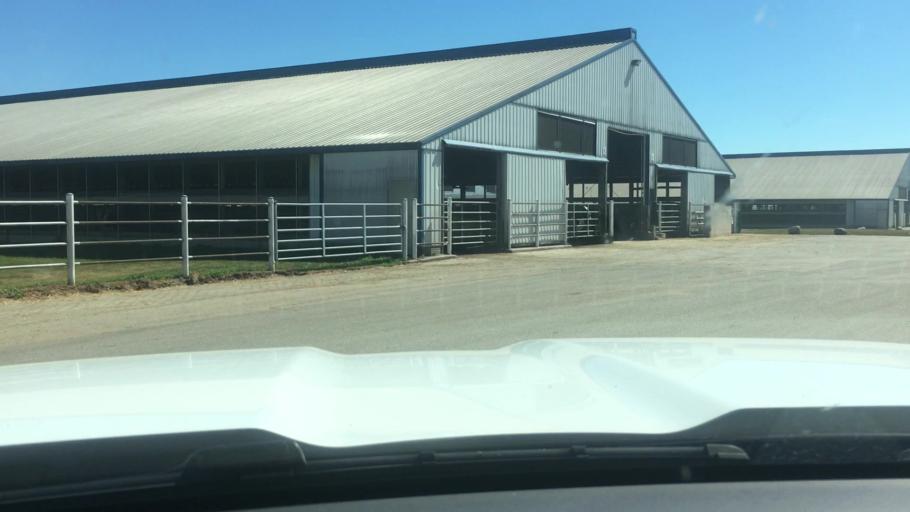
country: US
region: Michigan
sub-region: Montcalm County
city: Carson City
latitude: 43.2501
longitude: -84.7572
